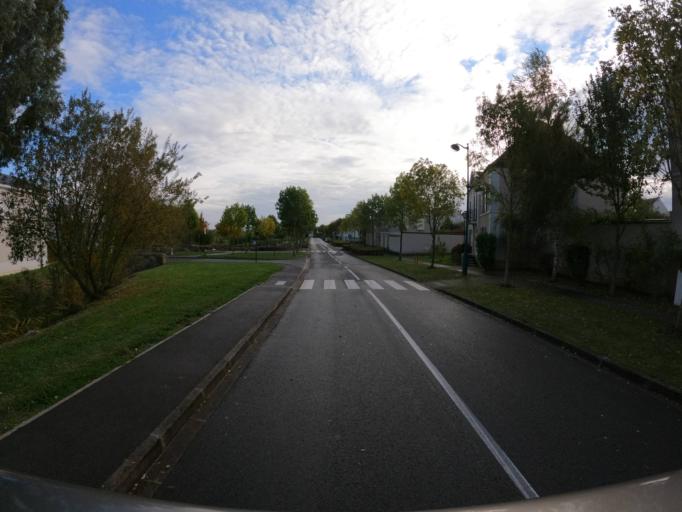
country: FR
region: Ile-de-France
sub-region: Departement de Seine-et-Marne
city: Magny-le-Hongre
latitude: 48.8748
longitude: 2.8165
